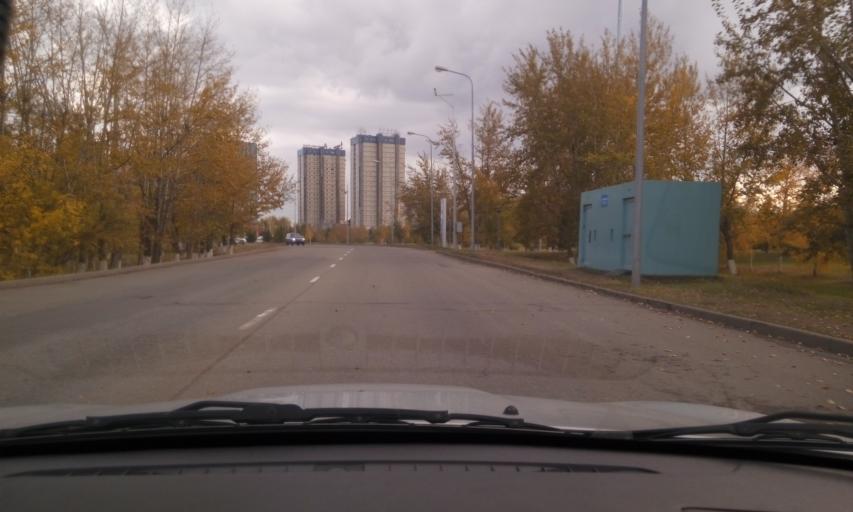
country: KZ
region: Astana Qalasy
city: Astana
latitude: 51.1502
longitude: 71.4205
